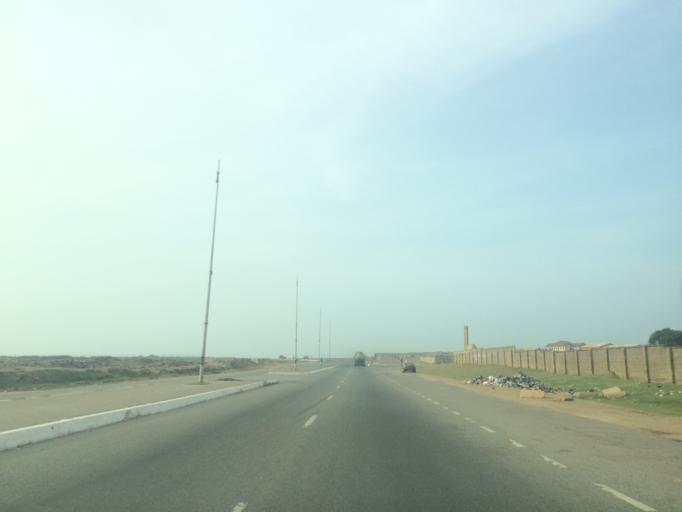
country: GH
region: Greater Accra
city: Accra
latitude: 5.5334
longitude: -0.2217
